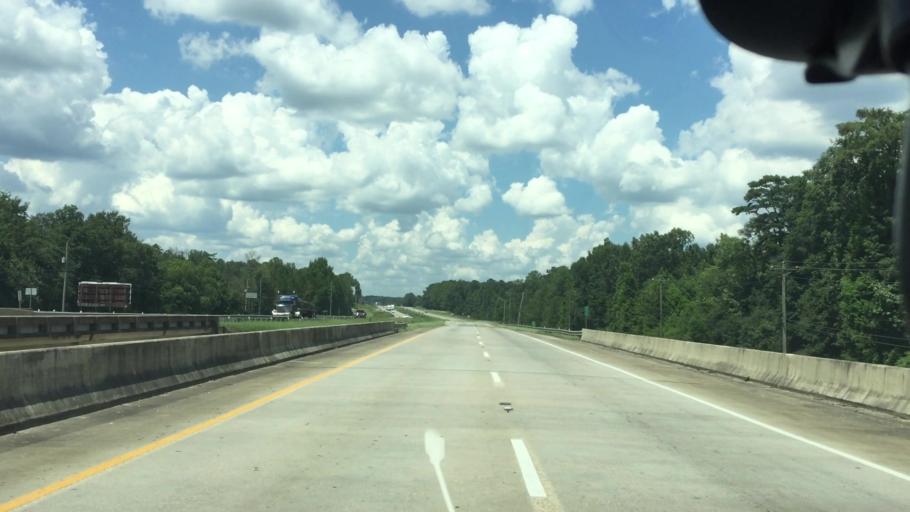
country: US
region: Alabama
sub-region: Pike County
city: Troy
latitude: 31.8448
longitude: -85.9947
